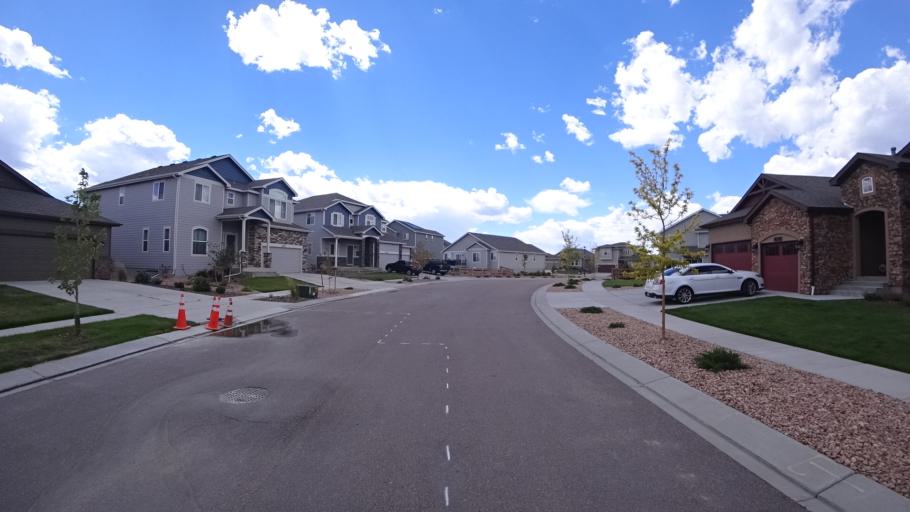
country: US
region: Colorado
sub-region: El Paso County
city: Black Forest
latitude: 38.9520
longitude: -104.7036
